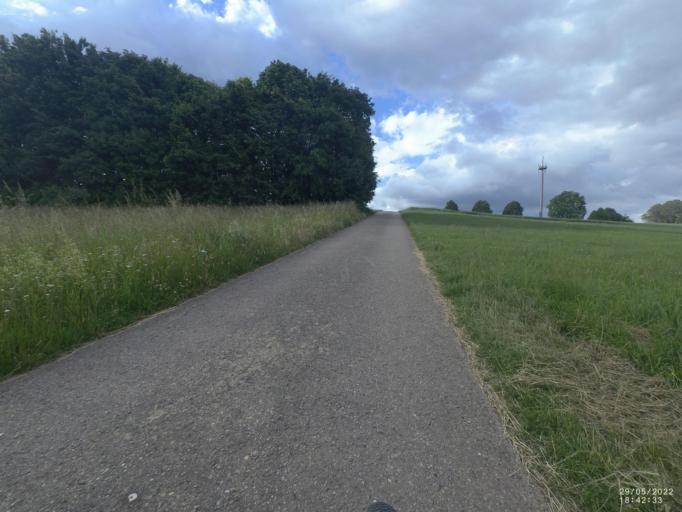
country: DE
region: Baden-Wuerttemberg
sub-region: Regierungsbezirk Stuttgart
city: Bolheim
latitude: 48.6006
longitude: 10.1072
